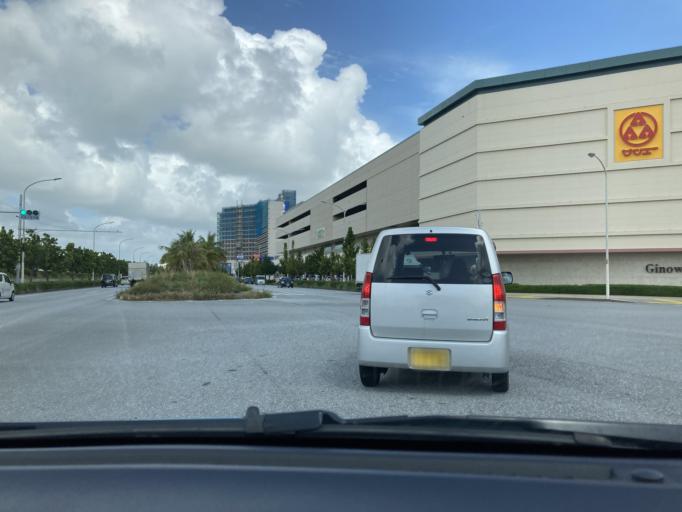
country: JP
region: Okinawa
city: Ginowan
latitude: 26.2748
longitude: 127.7284
